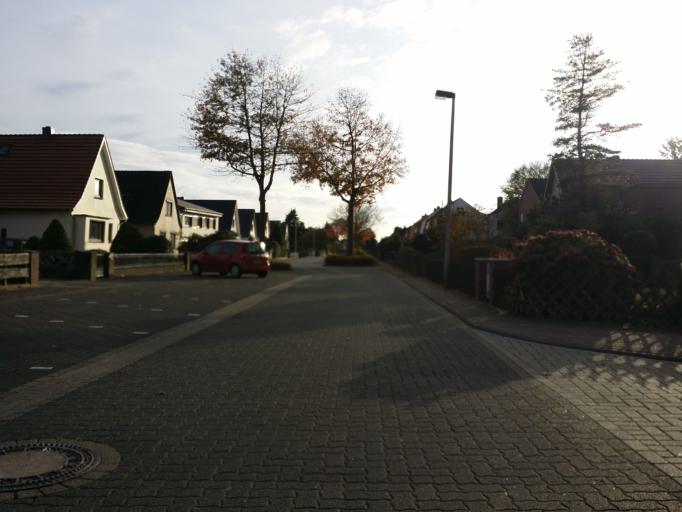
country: DE
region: Lower Saxony
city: Delmenhorst
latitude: 53.0425
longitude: 8.6707
